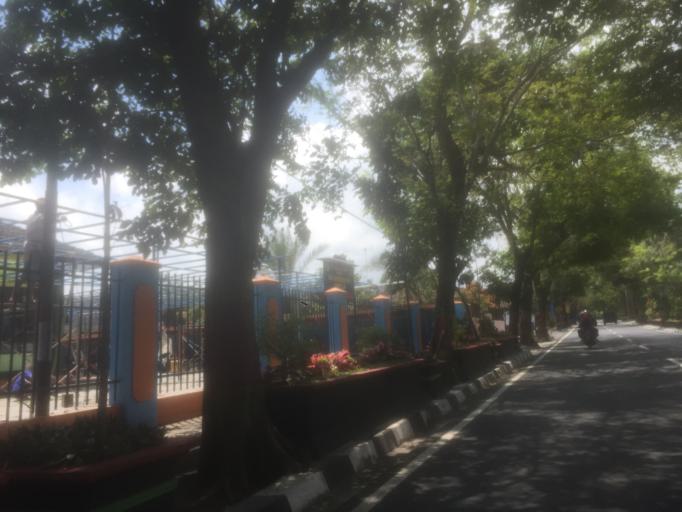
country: ID
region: Central Java
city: Muntilan
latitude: -7.5756
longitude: 110.2700
